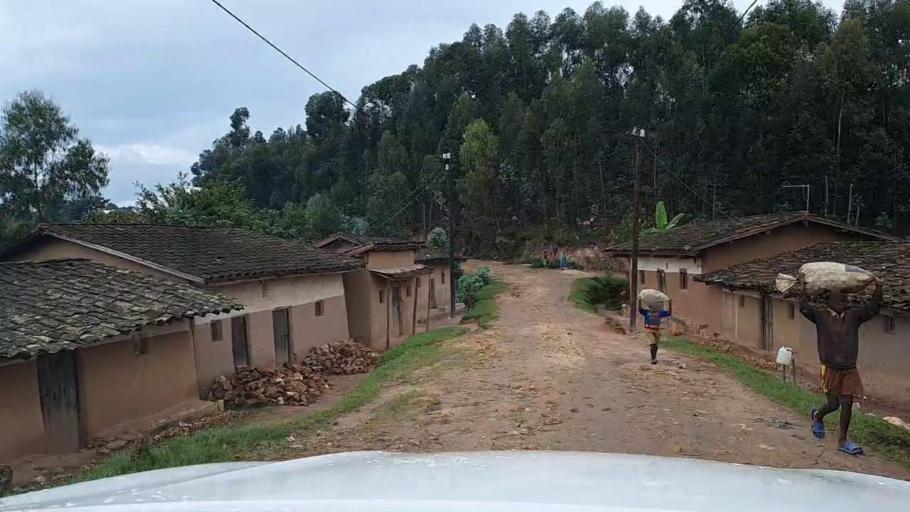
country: RW
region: Southern Province
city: Nzega
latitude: -2.4563
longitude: 29.4678
